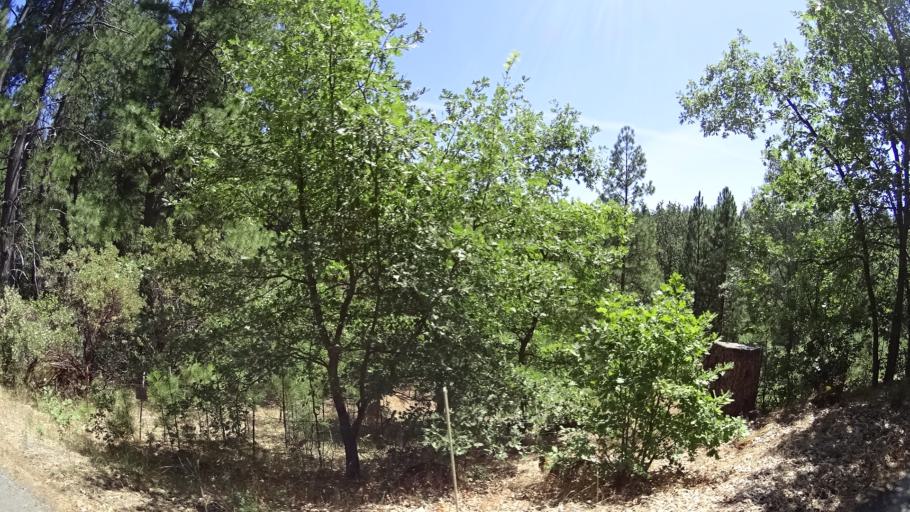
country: US
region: California
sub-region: Amador County
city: Pioneer
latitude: 38.4210
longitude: -120.5180
